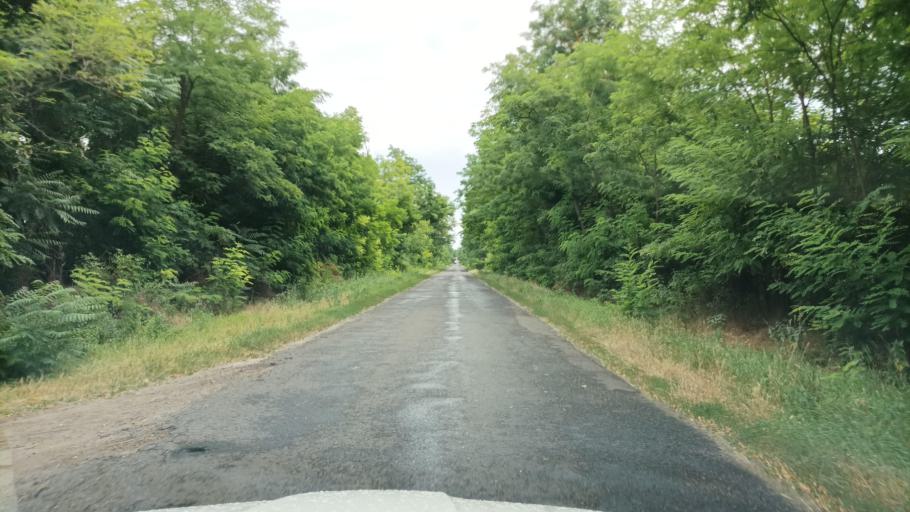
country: HU
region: Pest
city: Orkeny
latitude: 47.0474
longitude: 19.3370
